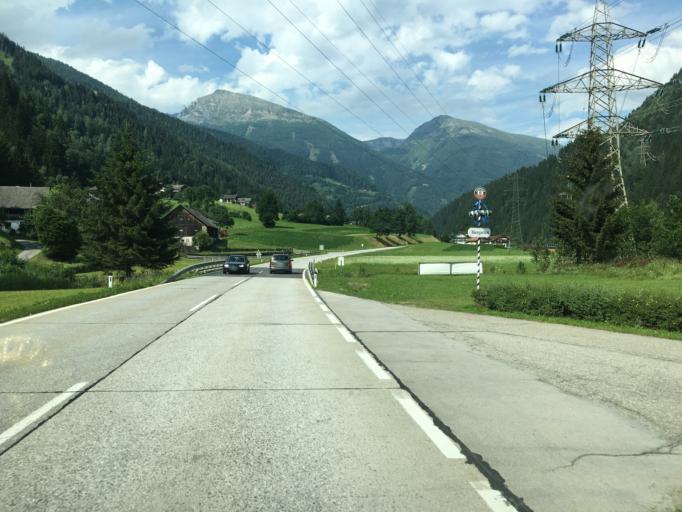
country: AT
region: Carinthia
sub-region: Politischer Bezirk Spittal an der Drau
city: Stall
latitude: 46.9143
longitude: 13.0698
